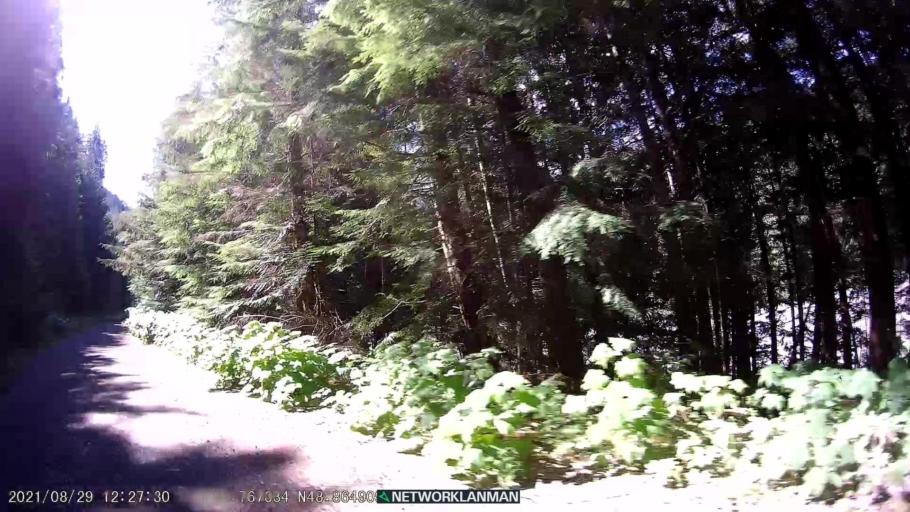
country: CA
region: British Columbia
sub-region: Fraser Valley Regional District
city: Chilliwack
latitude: 48.8648
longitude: -121.7674
